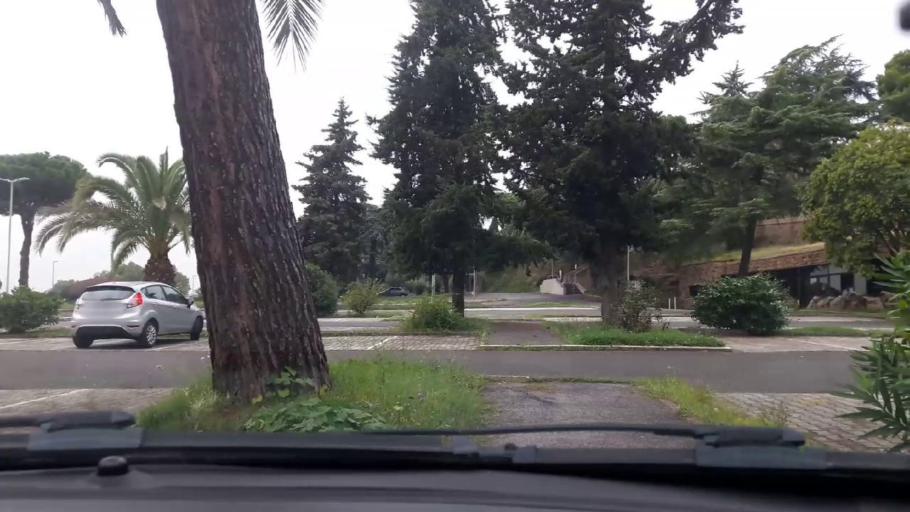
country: IT
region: Latium
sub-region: Citta metropolitana di Roma Capitale
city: Borgo Lotti
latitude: 41.7773
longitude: 12.5432
